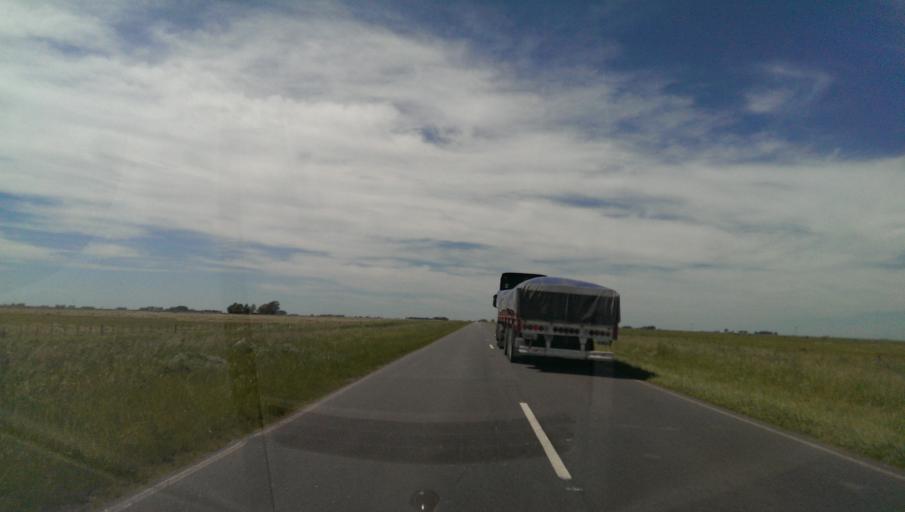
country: AR
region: Buenos Aires
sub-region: Partido de Laprida
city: Laprida
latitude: -37.2411
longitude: -60.7703
